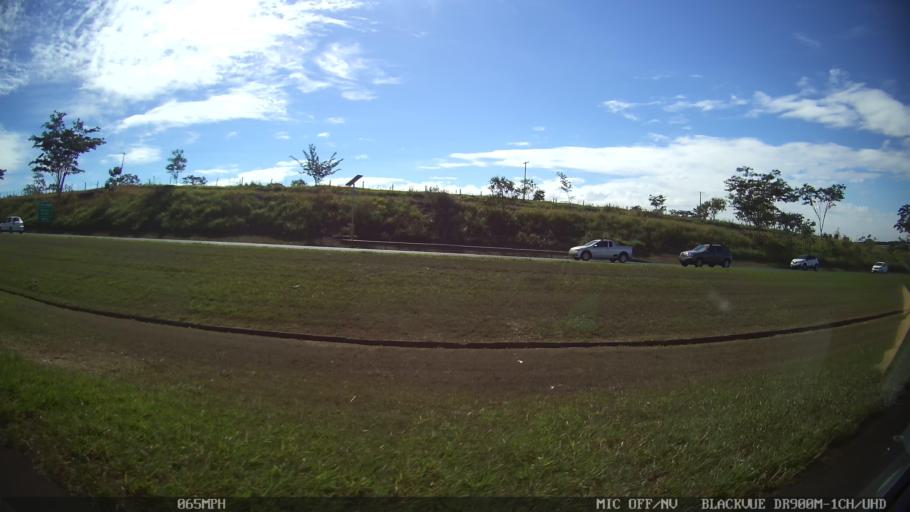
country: BR
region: Sao Paulo
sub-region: Sao Jose Do Rio Preto
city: Sao Jose do Rio Preto
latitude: -20.8146
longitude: -49.4713
